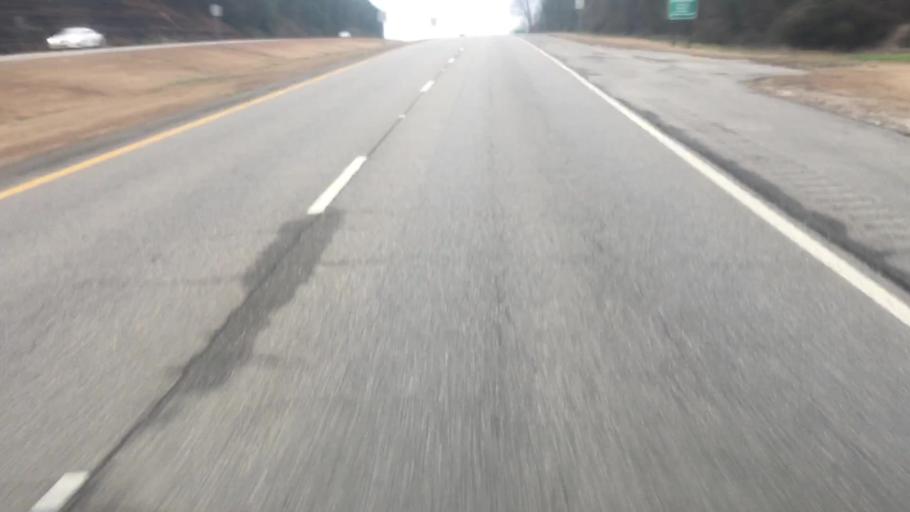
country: US
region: Alabama
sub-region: Walker County
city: Sumiton
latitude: 33.7668
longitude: -87.0705
